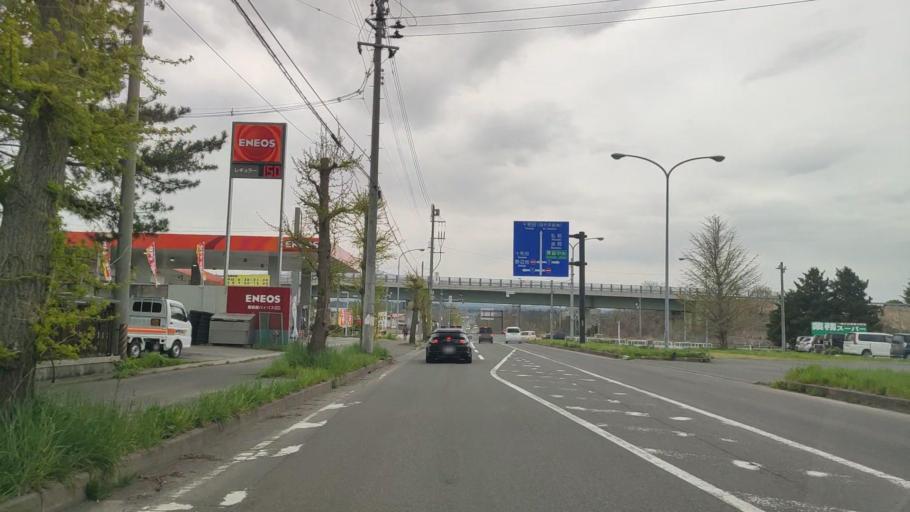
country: JP
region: Aomori
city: Aomori Shi
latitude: 40.7998
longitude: 140.7832
